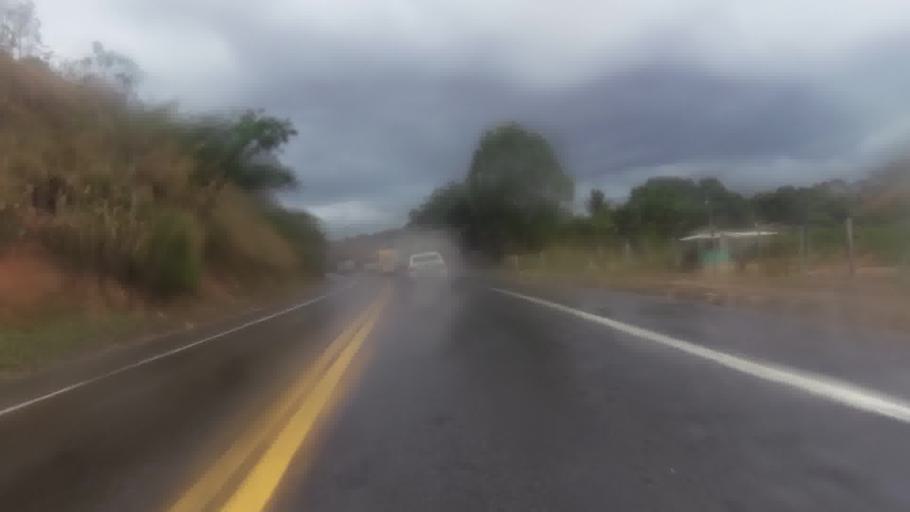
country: BR
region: Espirito Santo
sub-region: Cachoeiro De Itapemirim
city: Cachoeiro de Itapemirim
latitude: -20.9476
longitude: -41.0895
